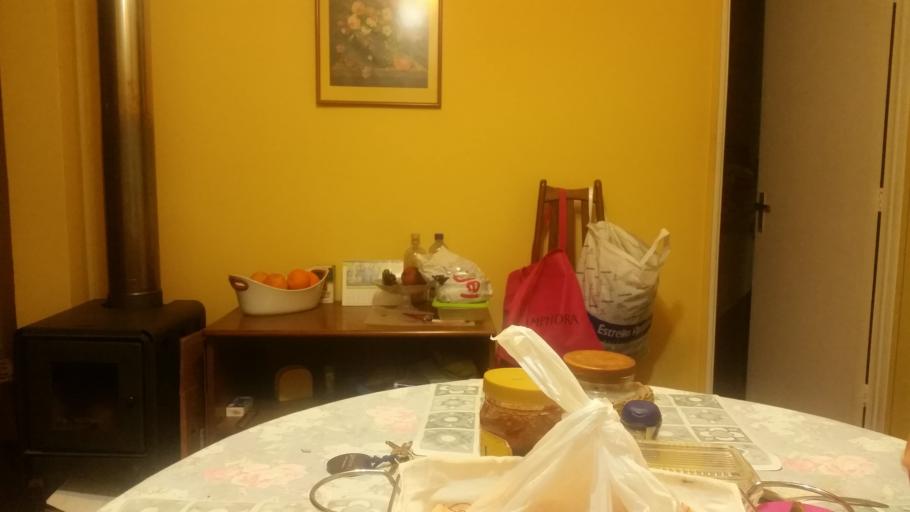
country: CL
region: Coquimbo
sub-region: Provincia de Elqui
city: La Serena
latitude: -29.9197
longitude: -71.2358
